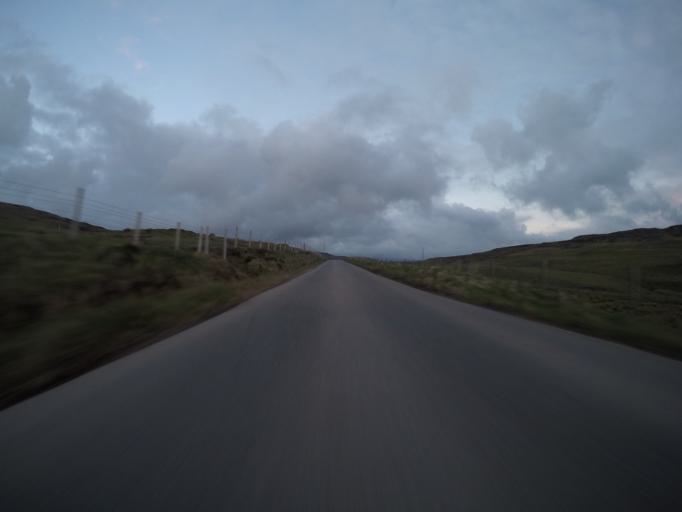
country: GB
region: Scotland
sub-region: Highland
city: Portree
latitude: 57.6008
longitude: -6.3771
